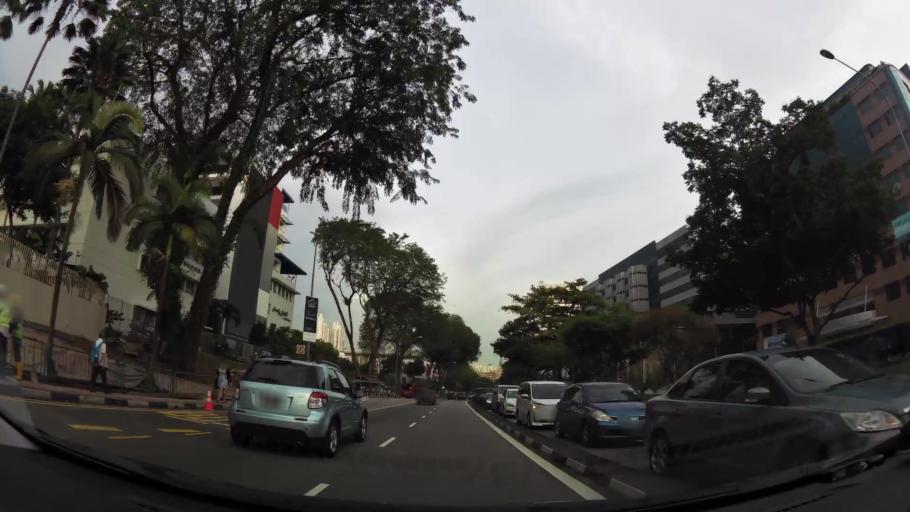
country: SG
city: Singapore
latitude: 1.2859
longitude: 103.8107
